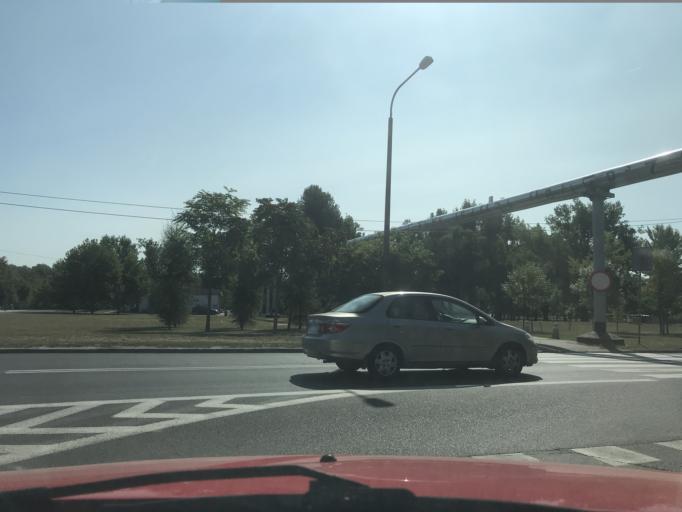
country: PL
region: Greater Poland Voivodeship
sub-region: Poznan
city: Poznan
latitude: 52.3898
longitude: 16.9243
